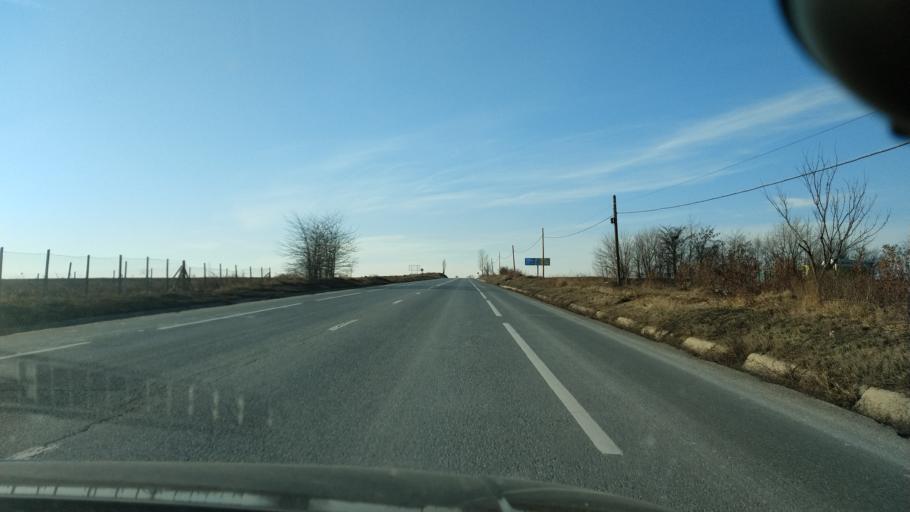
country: RO
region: Iasi
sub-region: Comuna Baltati
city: Baltati
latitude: 47.2211
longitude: 27.1393
